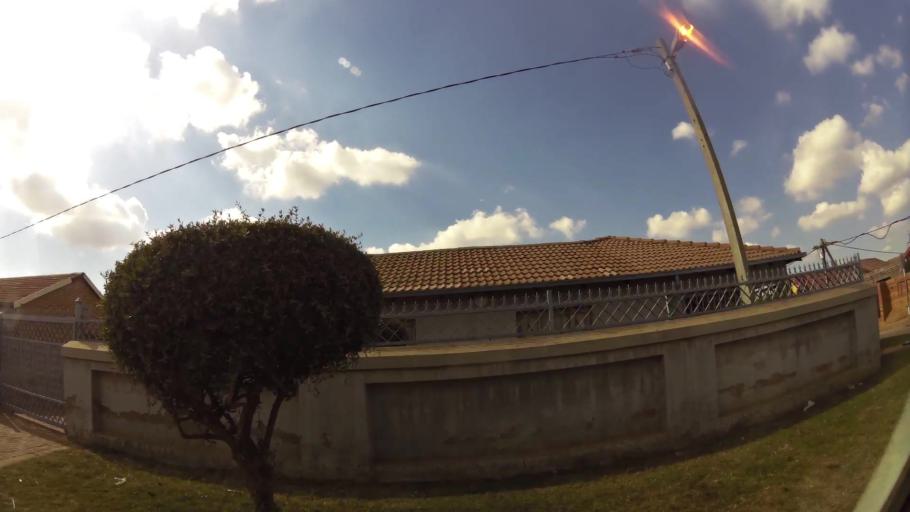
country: ZA
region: Gauteng
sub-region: City of Tshwane Metropolitan Municipality
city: Cullinan
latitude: -25.7077
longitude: 28.4152
